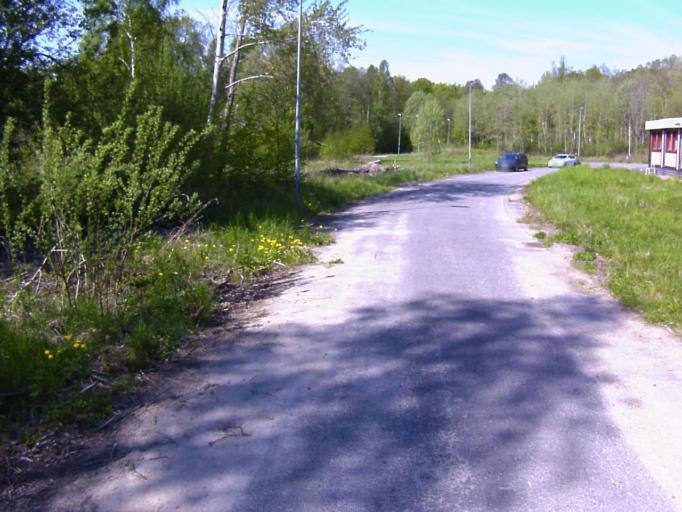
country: SE
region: Skane
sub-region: Kristianstads Kommun
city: Tollarp
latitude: 56.1728
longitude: 14.2997
